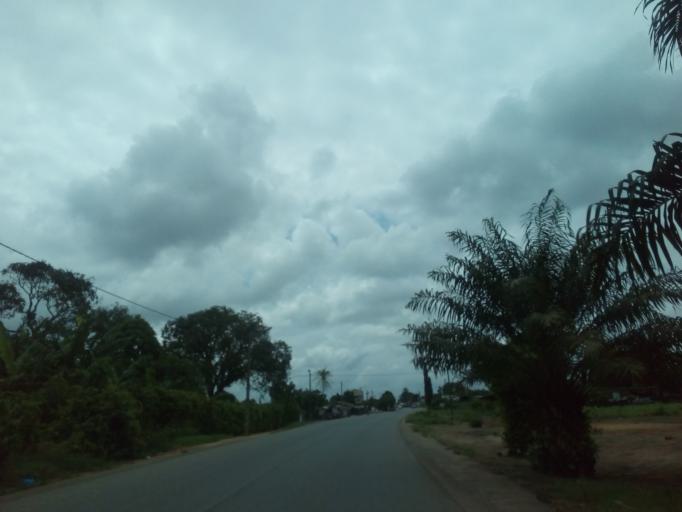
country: CI
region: Sud-Comoe
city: Aboisso
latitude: 5.4563
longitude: -3.2570
